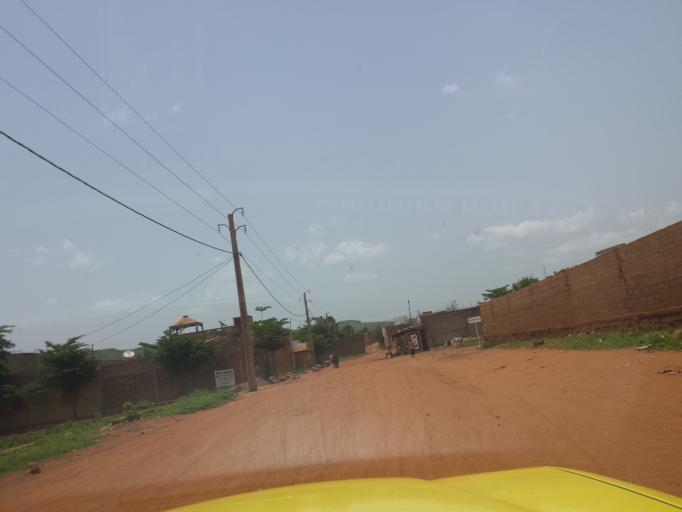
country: ML
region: Bamako
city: Bamako
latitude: 12.6086
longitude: -7.8893
